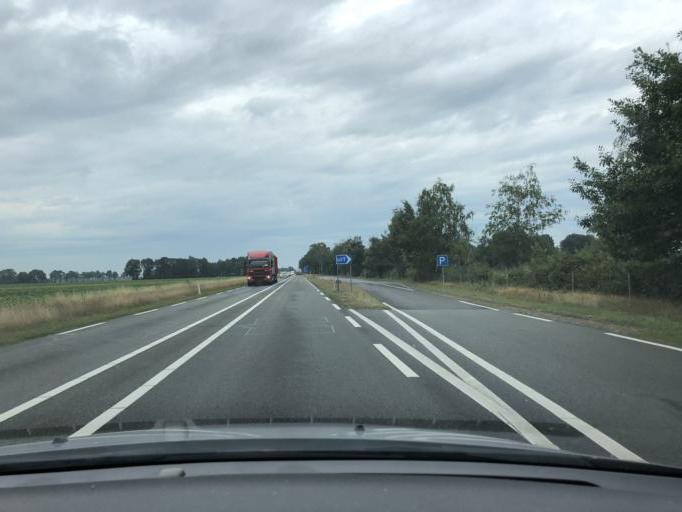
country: NL
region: Overijssel
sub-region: Gemeente Twenterand
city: Den Ham
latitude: 52.5436
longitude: 6.4149
